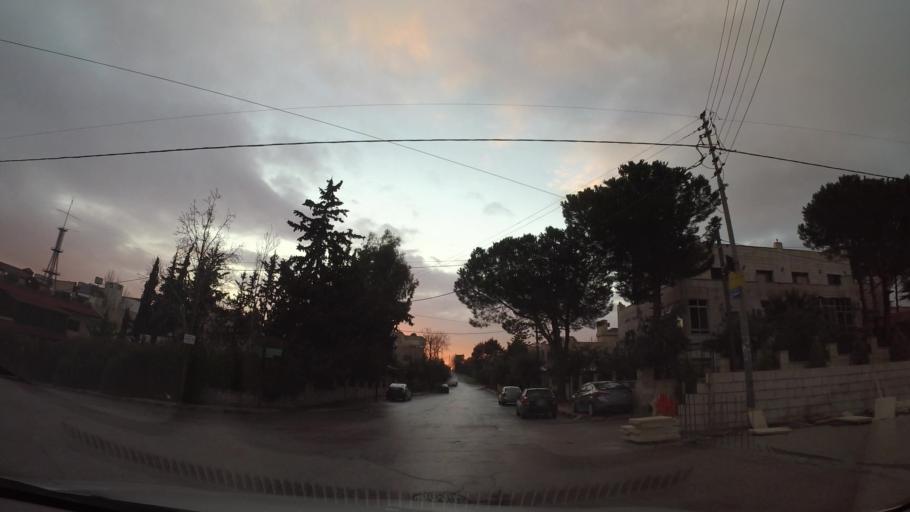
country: JO
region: Amman
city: Al Jubayhah
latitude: 32.0322
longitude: 35.8187
